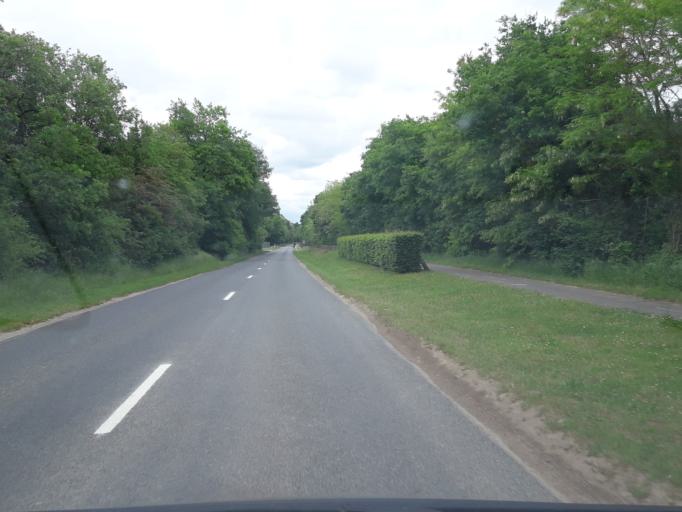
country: FR
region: Ile-de-France
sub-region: Departement de l'Essonne
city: Boissy-le-Cutte
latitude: 48.4415
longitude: 2.2953
